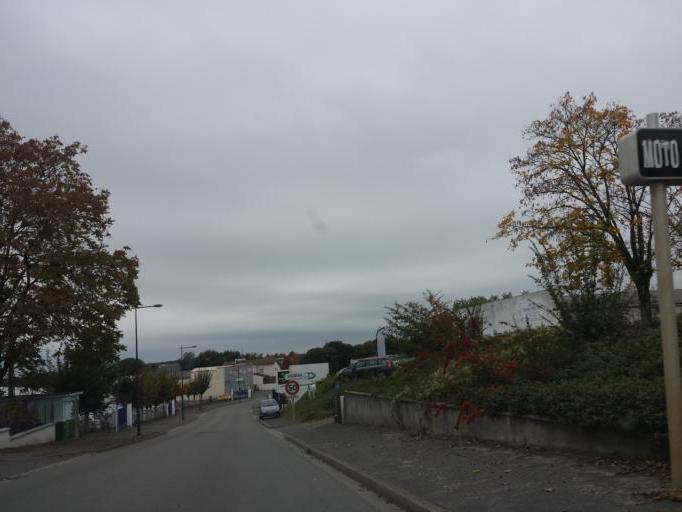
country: FR
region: Poitou-Charentes
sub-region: Departement de la Charente
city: Angouleme
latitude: 45.6251
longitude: 0.1567
